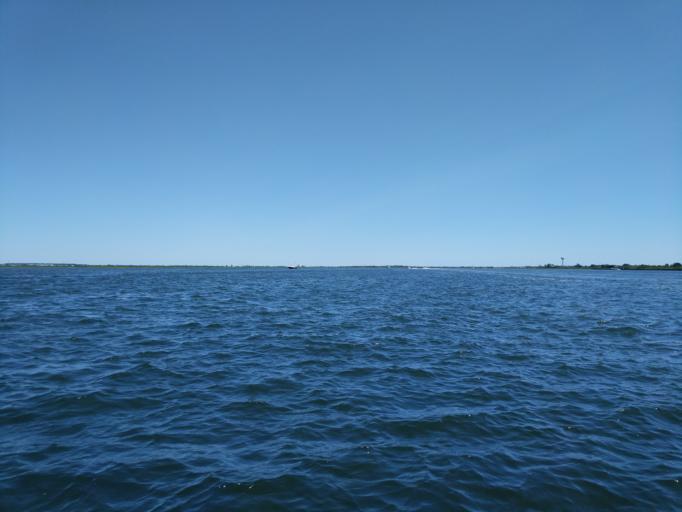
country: US
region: New York
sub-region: Nassau County
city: Lido Beach
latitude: 40.5962
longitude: -73.6258
